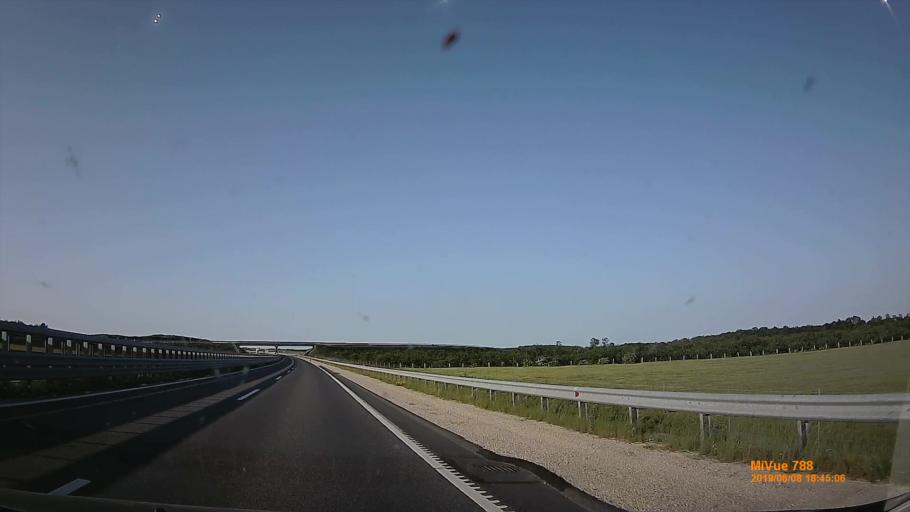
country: HU
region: Gyor-Moson-Sopron
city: Beled
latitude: 47.4745
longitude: 17.1382
